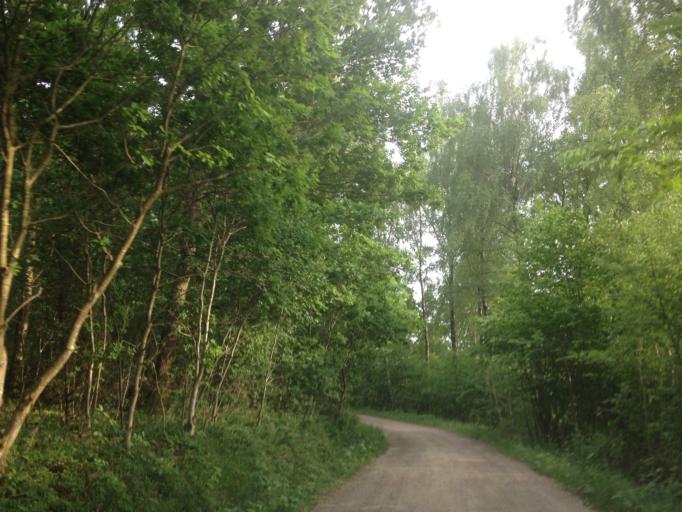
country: SE
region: Vaestra Goetaland
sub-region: Kungalvs Kommun
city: Kungalv
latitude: 57.8177
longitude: 11.9305
